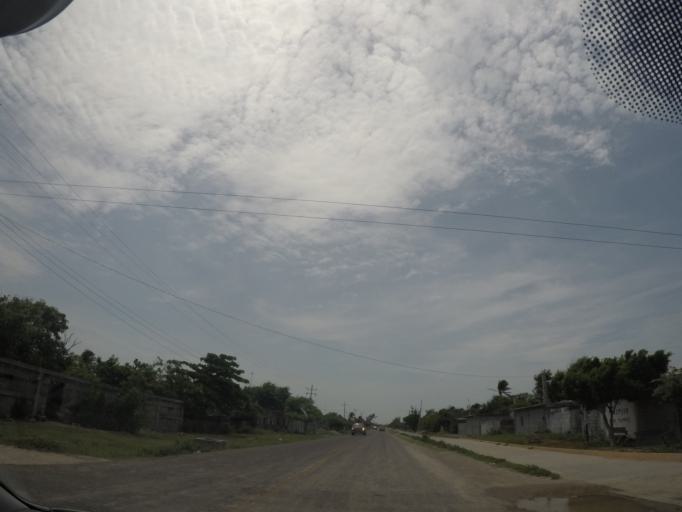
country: MX
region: Oaxaca
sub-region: San Mateo del Mar
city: Colonia Juarez
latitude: 16.2092
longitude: -95.0311
